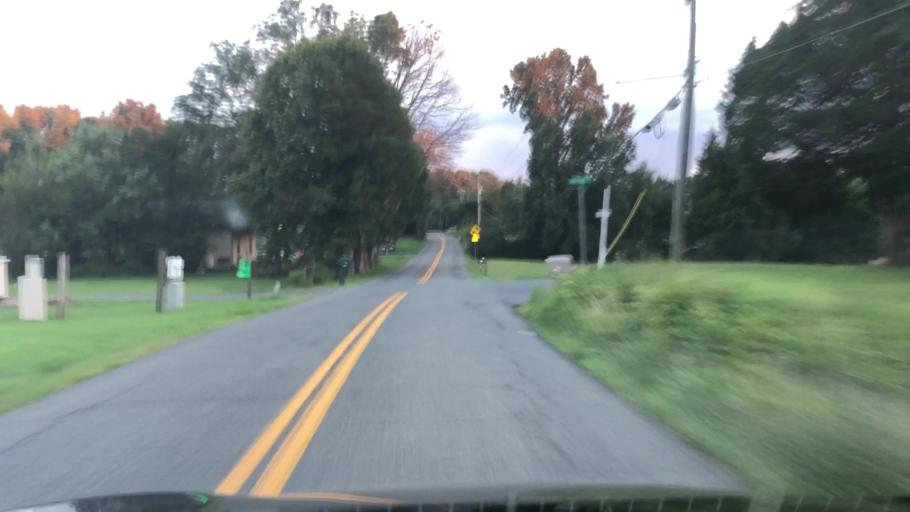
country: US
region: Virginia
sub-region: Stafford County
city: Stafford
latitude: 38.4767
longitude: -77.5799
